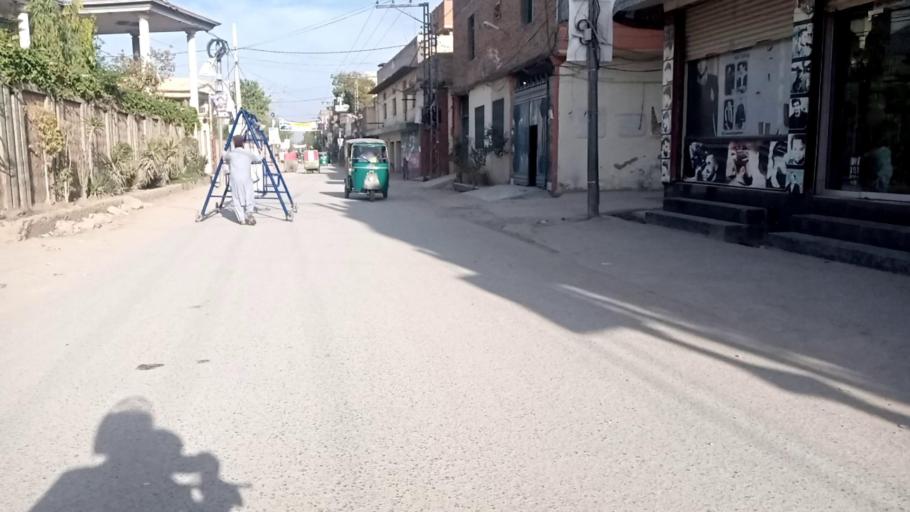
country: PK
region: Khyber Pakhtunkhwa
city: Peshawar
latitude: 34.0110
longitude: 71.6034
